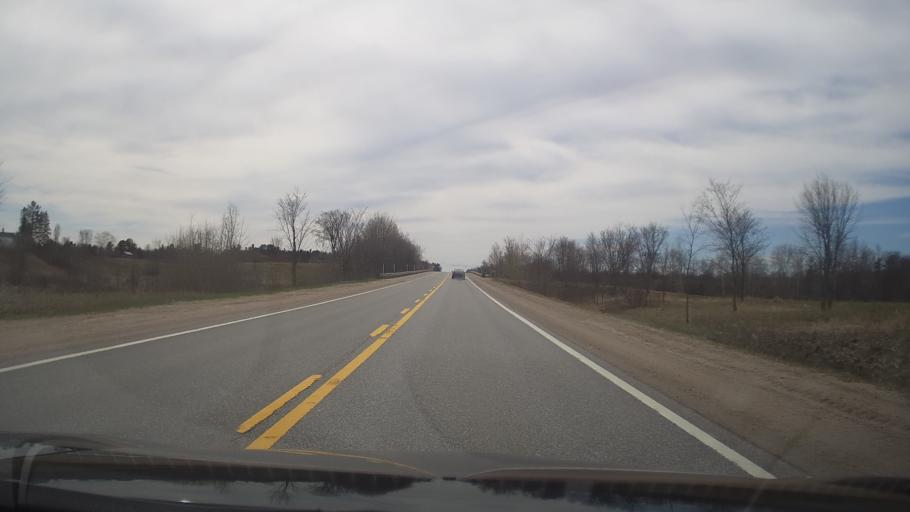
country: CA
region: Ontario
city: Arnprior
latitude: 45.5256
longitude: -76.2759
